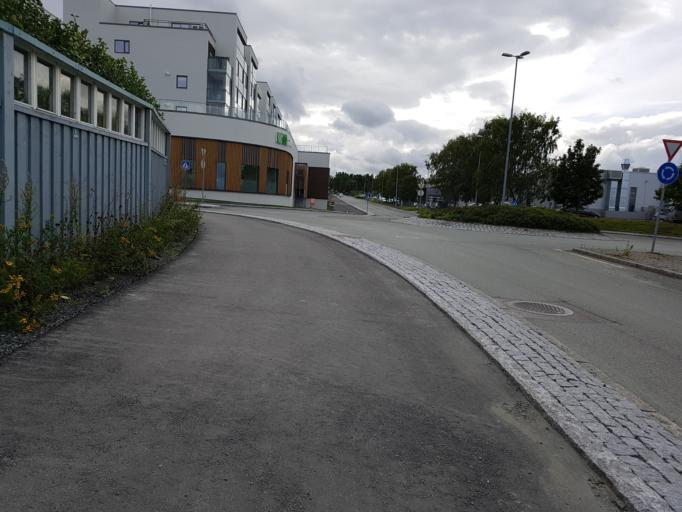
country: NO
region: Sor-Trondelag
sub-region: Trondheim
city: Trondheim
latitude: 63.4193
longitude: 10.4660
